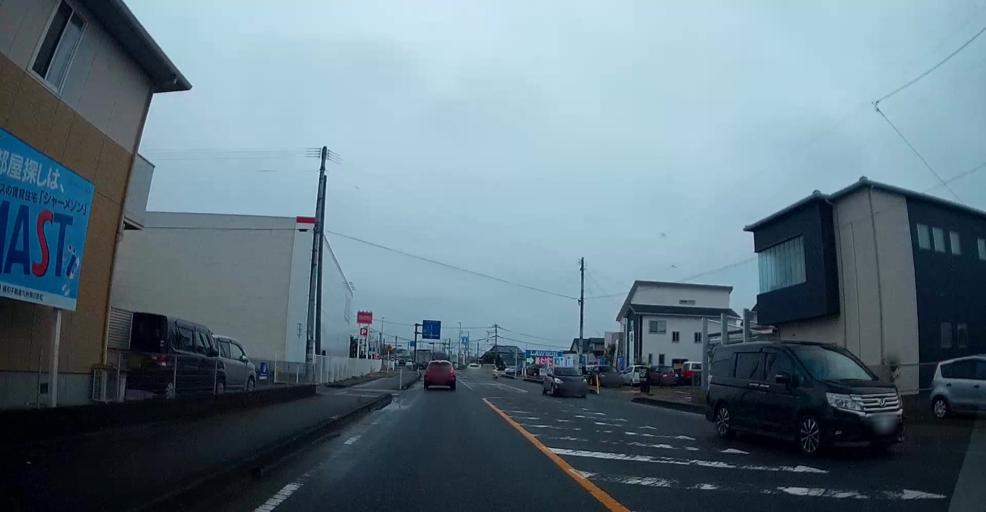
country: JP
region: Kumamoto
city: Kumamoto
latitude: 32.7412
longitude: 130.7404
